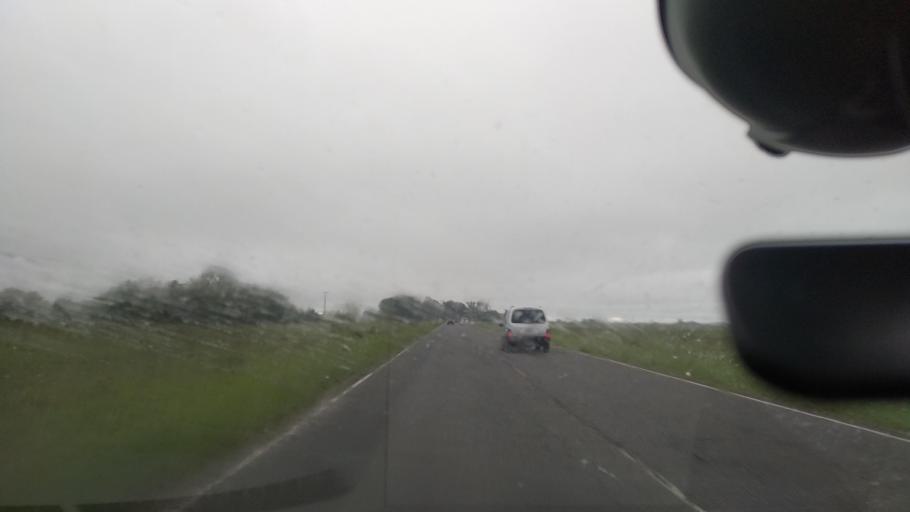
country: AR
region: Buenos Aires
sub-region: Partido de Magdalena
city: Magdalena
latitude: -35.2152
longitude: -57.7478
